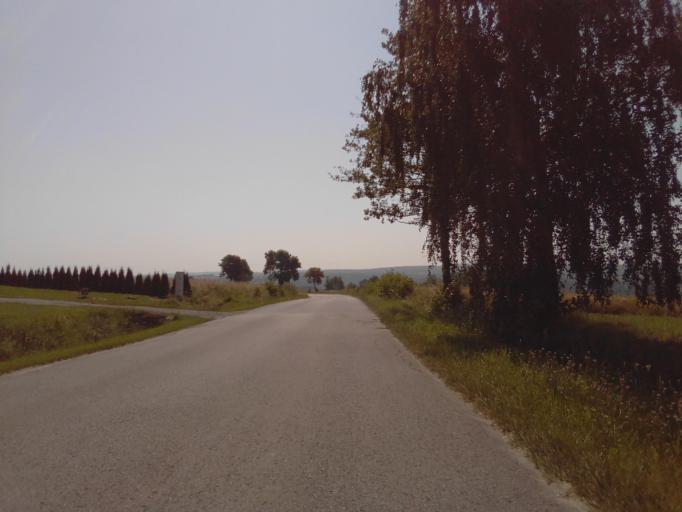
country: PL
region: Subcarpathian Voivodeship
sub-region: Powiat ropczycko-sedziszowski
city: Ropczyce
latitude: 50.0115
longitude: 21.6263
